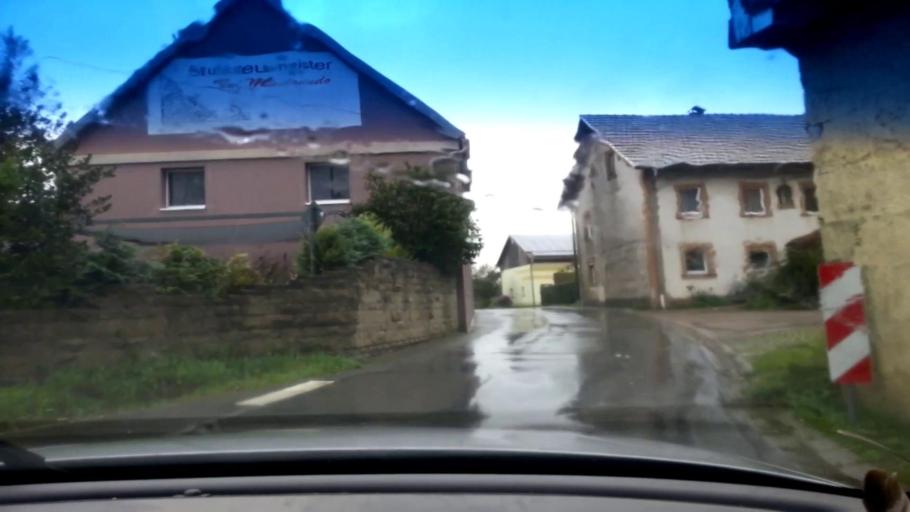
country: DE
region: Bavaria
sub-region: Upper Franconia
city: Wattendorf
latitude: 50.0329
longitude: 11.1267
